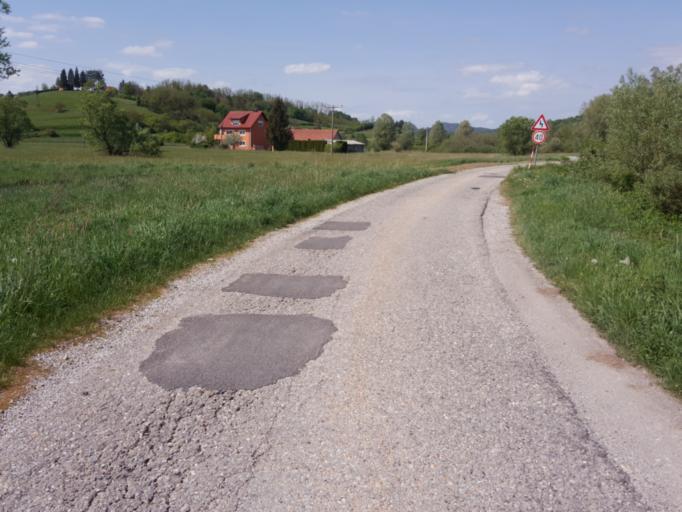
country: HR
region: Varazdinska
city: Lepoglava
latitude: 46.2279
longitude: 15.9655
